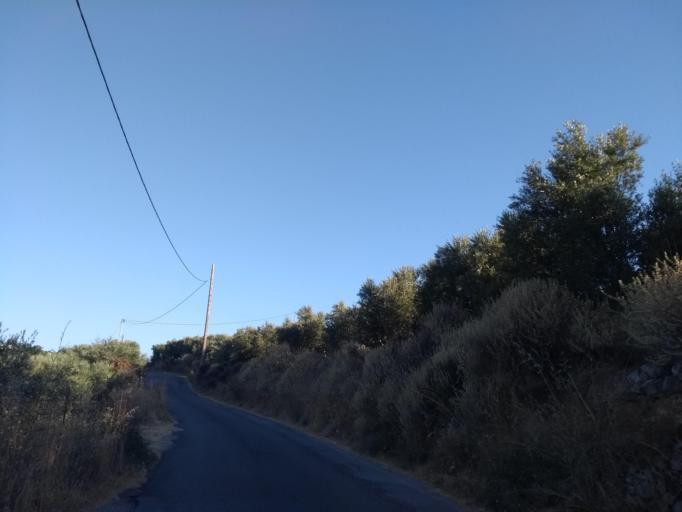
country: GR
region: Crete
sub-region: Nomos Chanias
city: Kalivai
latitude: 35.4328
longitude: 24.1756
